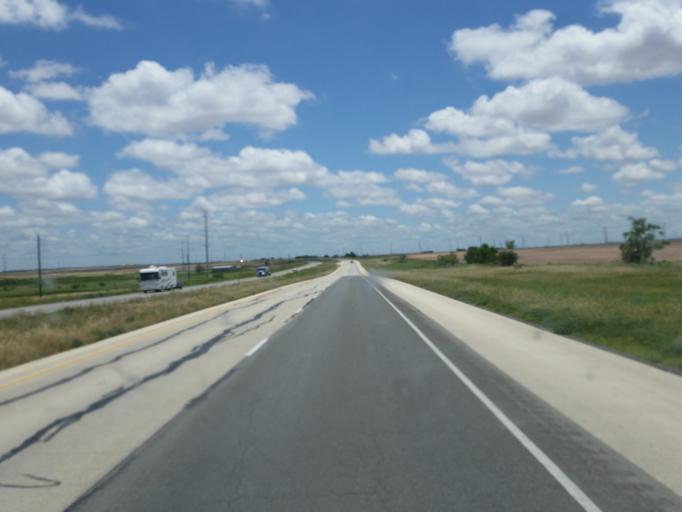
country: US
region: Texas
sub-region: Nolan County
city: Roscoe
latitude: 32.4954
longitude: -100.6367
